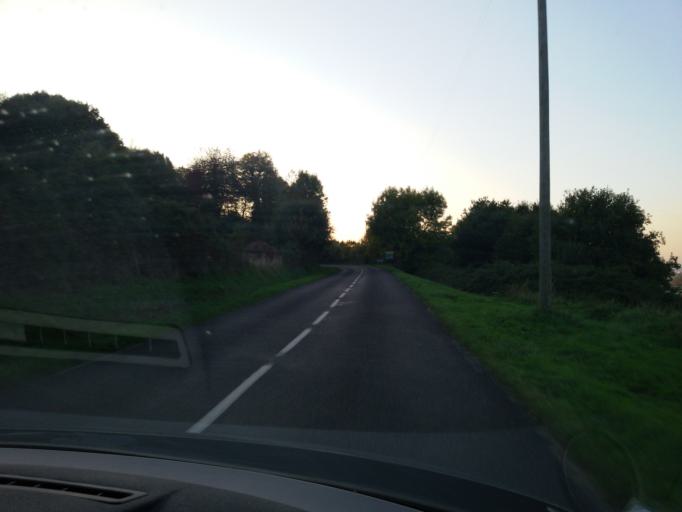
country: FR
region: Lower Normandy
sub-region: Departement du Calvados
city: Ablon
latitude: 49.4312
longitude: 0.3525
